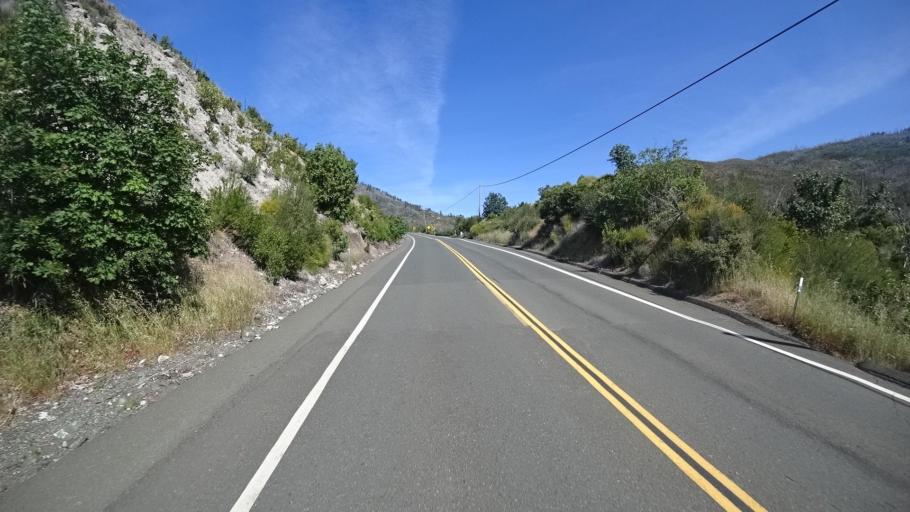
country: US
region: California
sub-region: Lake County
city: Cobb
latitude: 38.7914
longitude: -122.6955
